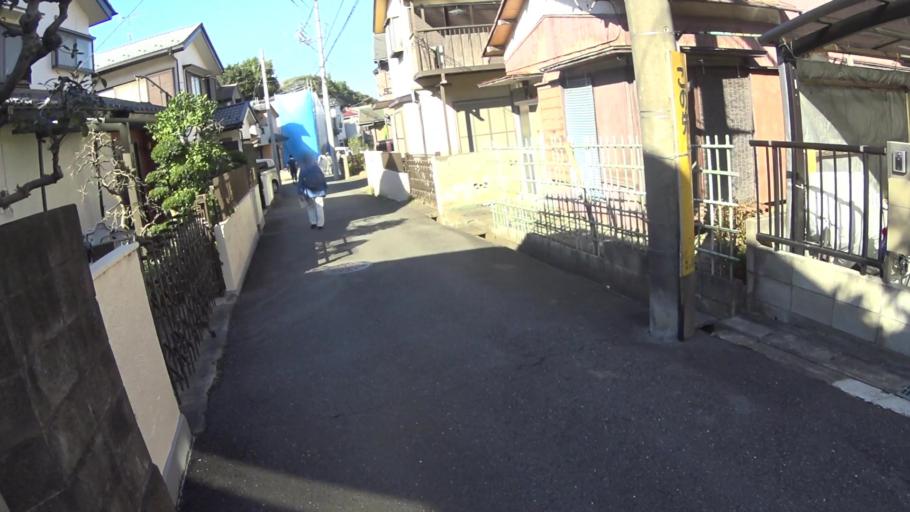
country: JP
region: Tokyo
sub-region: Machida-shi
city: Machida
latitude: 35.5583
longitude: 139.4463
